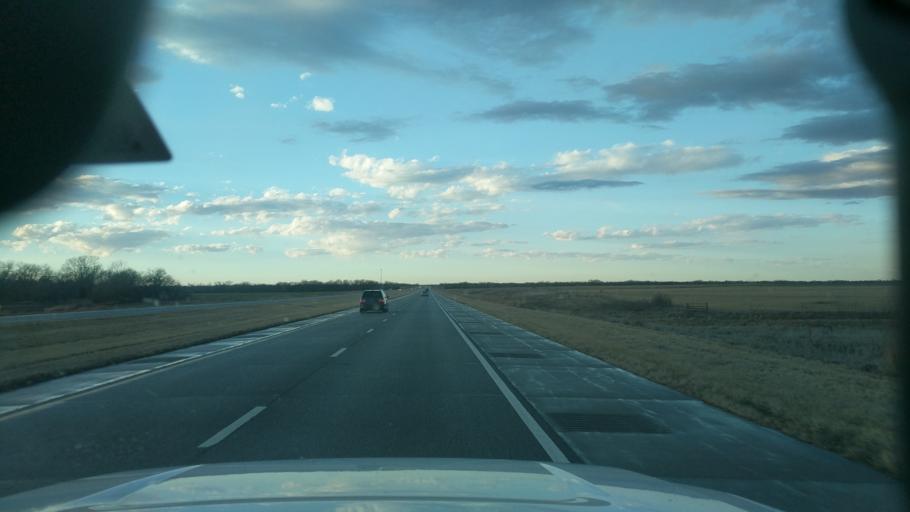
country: US
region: Kansas
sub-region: Harvey County
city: Hesston
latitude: 38.1770
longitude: -97.4512
